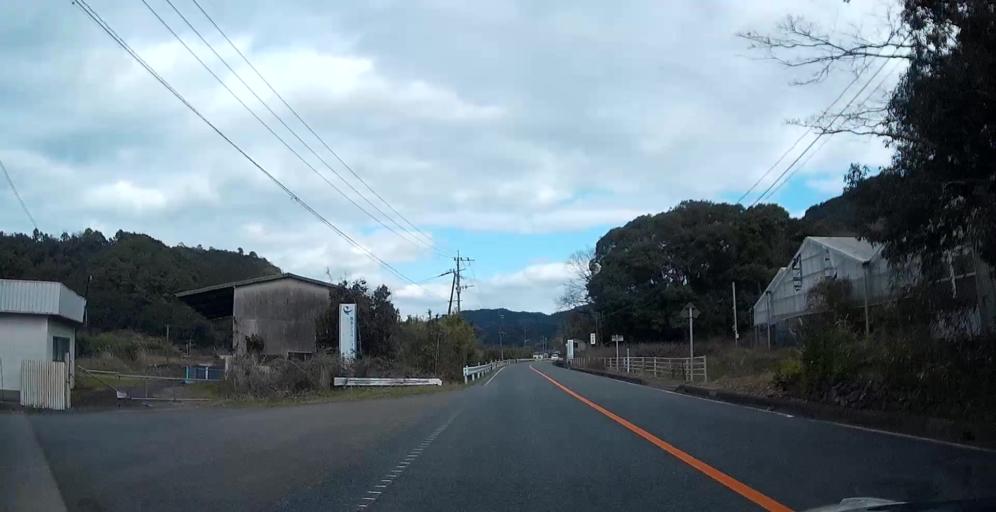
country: JP
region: Kumamoto
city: Minamata
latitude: 32.3401
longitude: 130.4951
